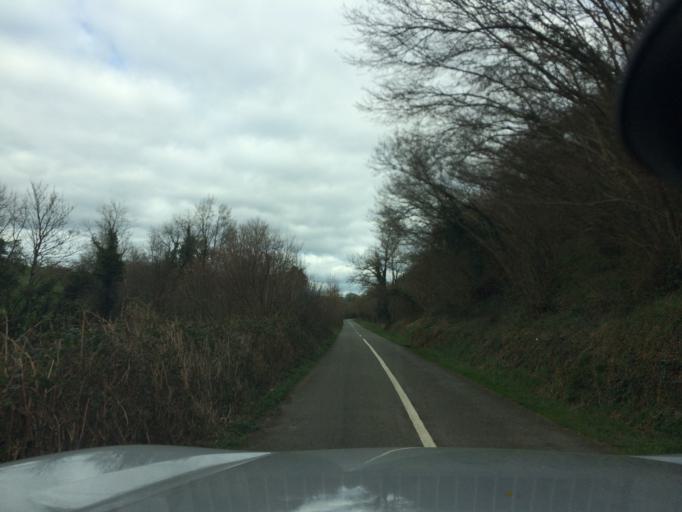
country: IE
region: Munster
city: Carrick-on-Suir
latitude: 52.2787
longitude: -7.4269
